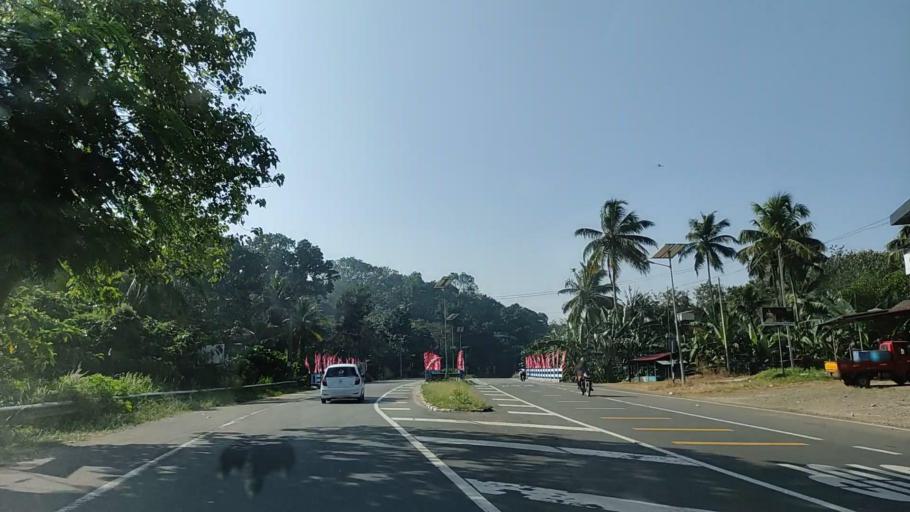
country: IN
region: Kerala
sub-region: Kollam
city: Punalur
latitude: 8.9096
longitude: 76.8550
